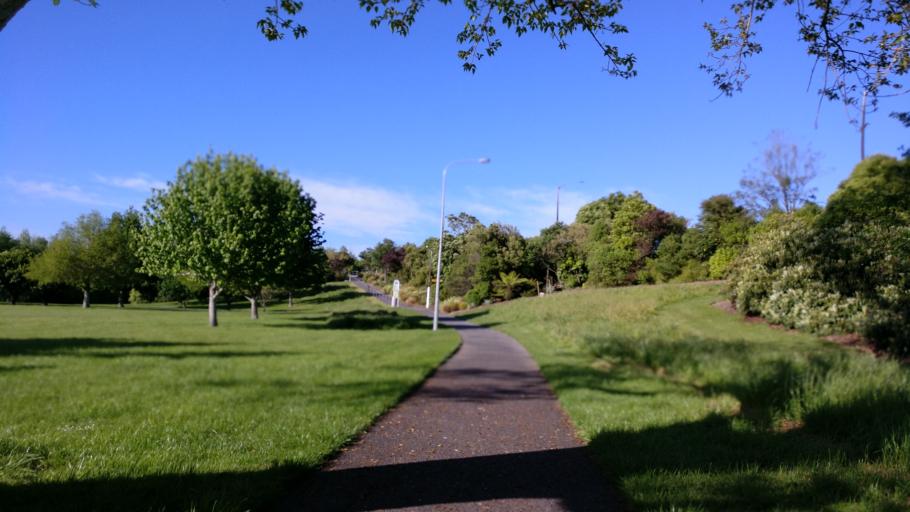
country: NZ
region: Wellington
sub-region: Lower Hutt City
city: Lower Hutt
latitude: -41.1905
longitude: 174.9307
